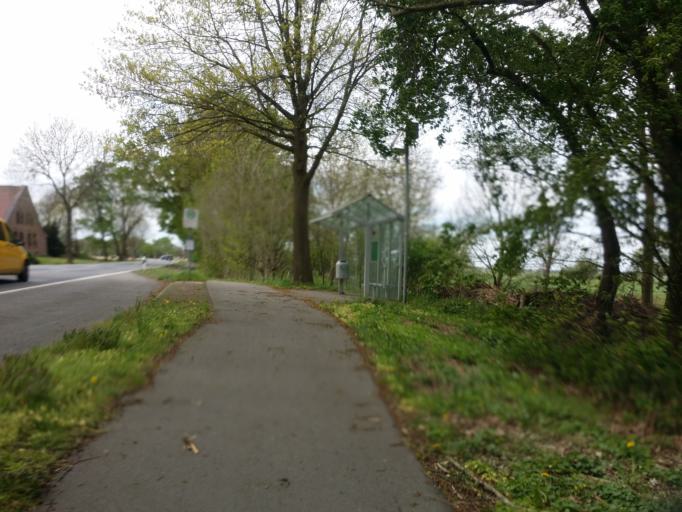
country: DE
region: Lower Saxony
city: Lemwerder
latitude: 53.1419
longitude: 8.5886
